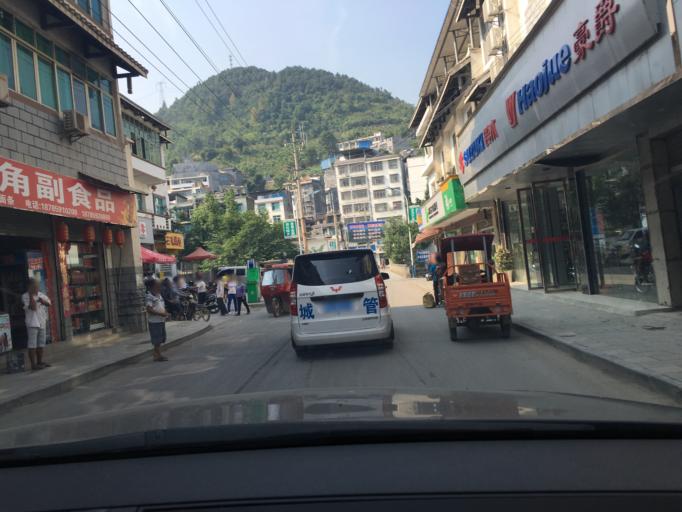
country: CN
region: Guangxi Zhuangzu Zizhiqu
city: Xinzhou
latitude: 24.9860
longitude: 105.8045
